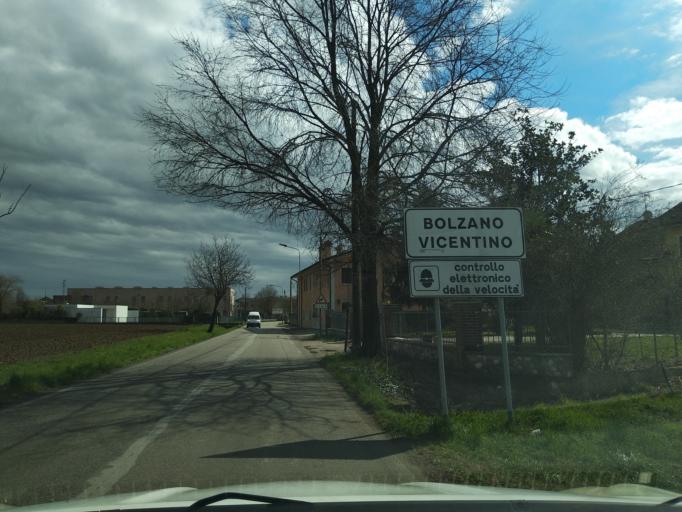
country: IT
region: Veneto
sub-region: Provincia di Vicenza
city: Bolzano Vicentino
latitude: 45.6083
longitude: 11.6083
